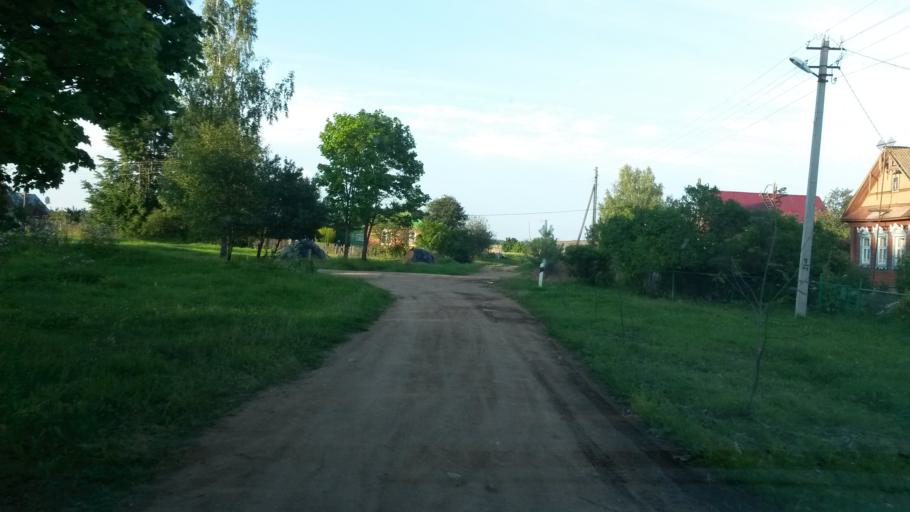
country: RU
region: Jaroslavl
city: Gavrilov-Yam
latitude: 57.3069
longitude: 39.9480
